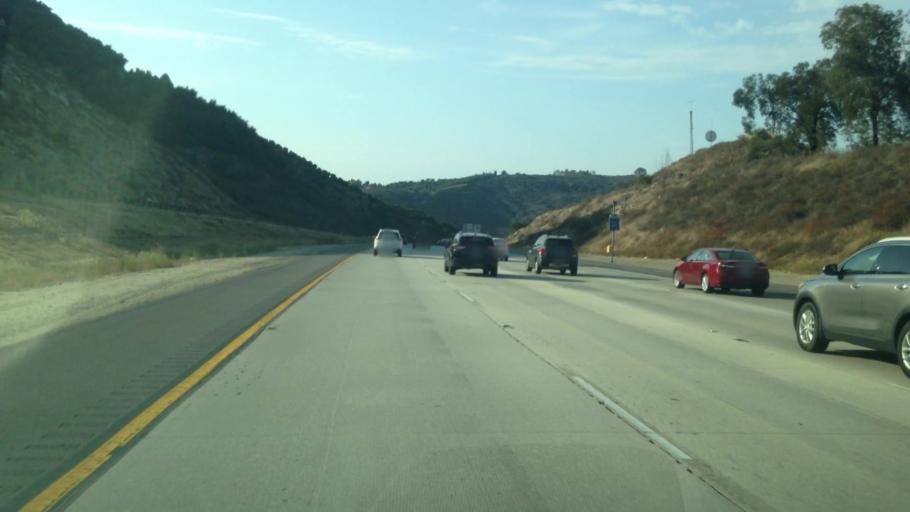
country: US
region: California
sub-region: San Diego County
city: Hidden Meadows
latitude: 33.2569
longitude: -117.1575
